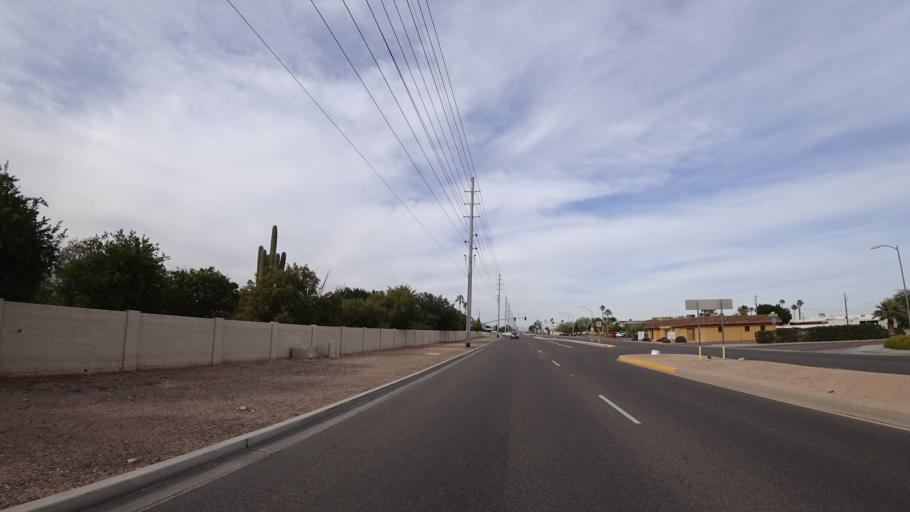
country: US
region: Arizona
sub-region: Maricopa County
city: Sun City
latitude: 33.5791
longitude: -112.2727
